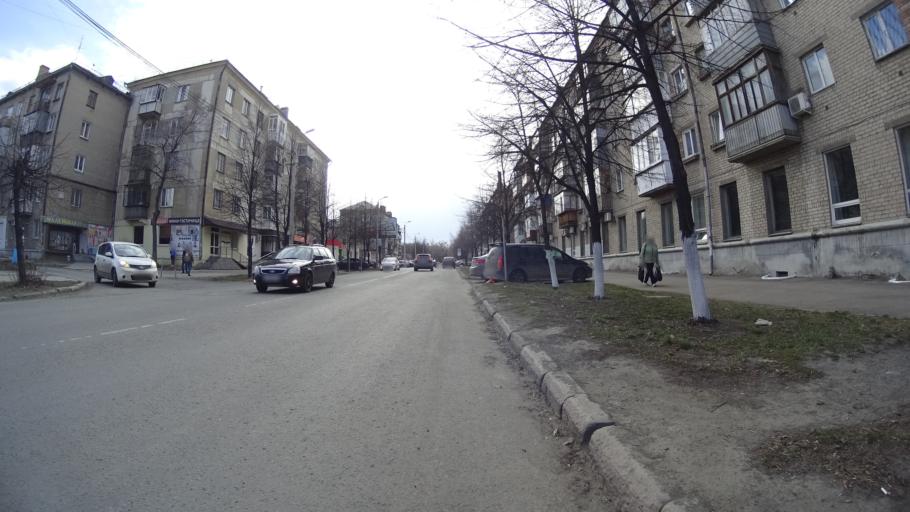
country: RU
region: Chelyabinsk
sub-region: Gorod Chelyabinsk
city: Chelyabinsk
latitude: 55.1554
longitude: 61.4101
